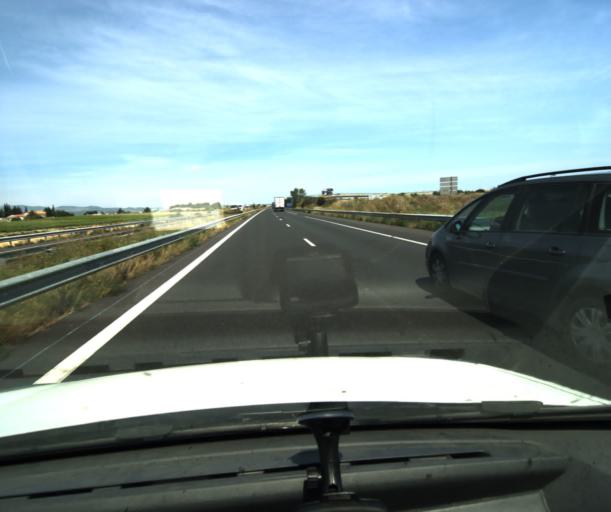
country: FR
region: Languedoc-Roussillon
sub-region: Departement des Pyrenees-Orientales
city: Peyrestortes
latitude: 42.7335
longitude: 2.8825
